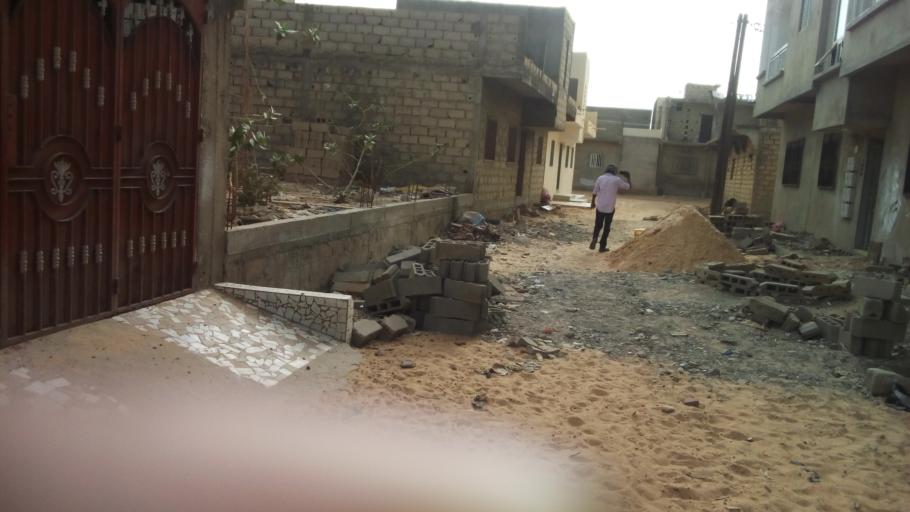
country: SN
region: Dakar
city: Pikine
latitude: 14.8001
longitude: -17.3402
